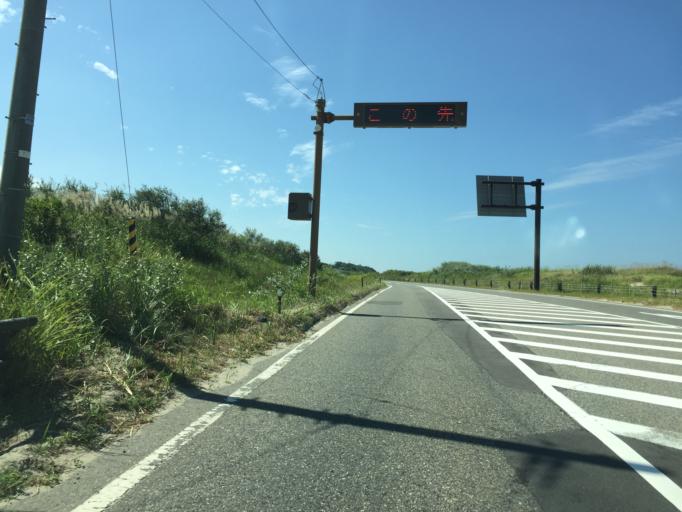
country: JP
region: Niigata
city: Niigata-shi
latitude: 37.9403
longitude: 139.0544
